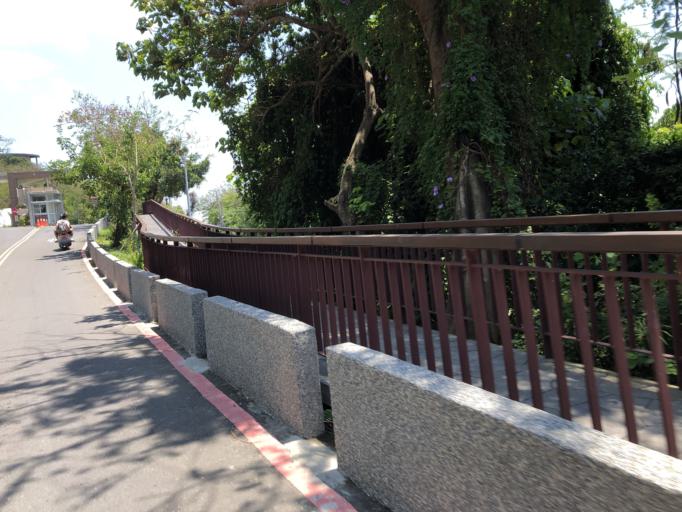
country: TW
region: Kaohsiung
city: Kaohsiung
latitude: 22.6270
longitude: 120.2704
